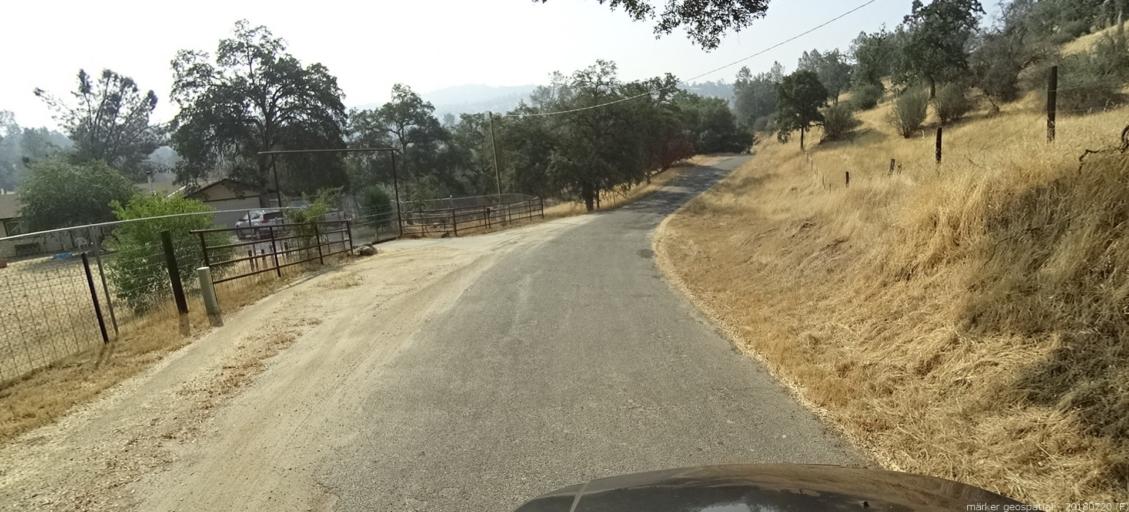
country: US
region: California
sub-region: Madera County
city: Yosemite Lakes
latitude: 37.2951
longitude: -119.8672
